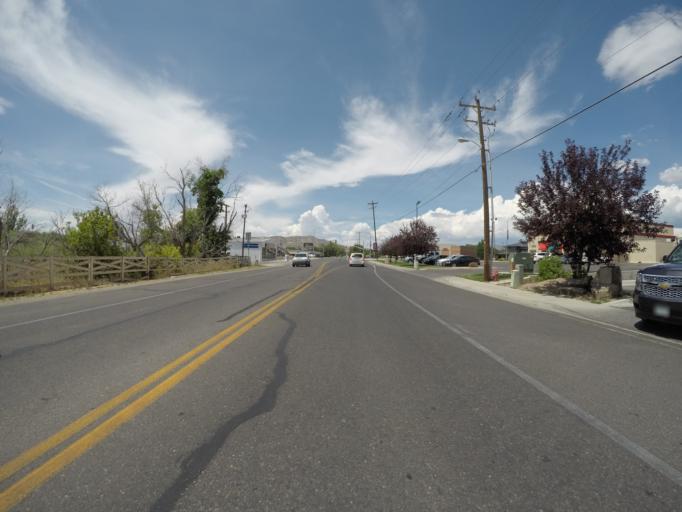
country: US
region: Utah
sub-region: Uintah County
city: Vernal
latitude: 40.4483
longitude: -109.5517
